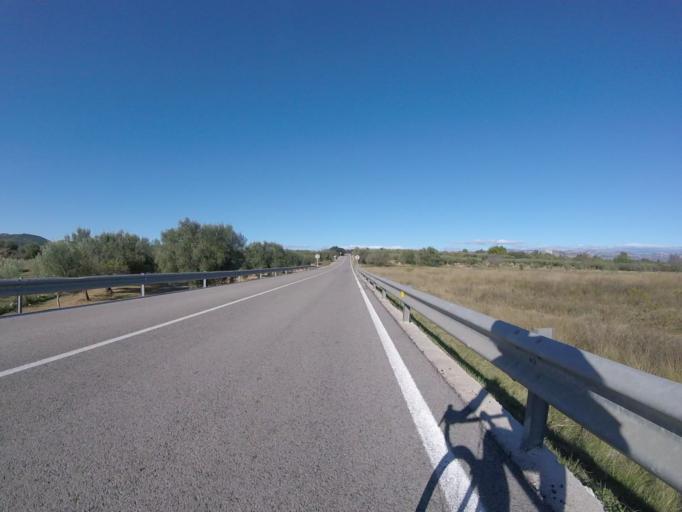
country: ES
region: Valencia
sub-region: Provincia de Castello
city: Cervera del Maestre
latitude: 40.4728
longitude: 0.2372
